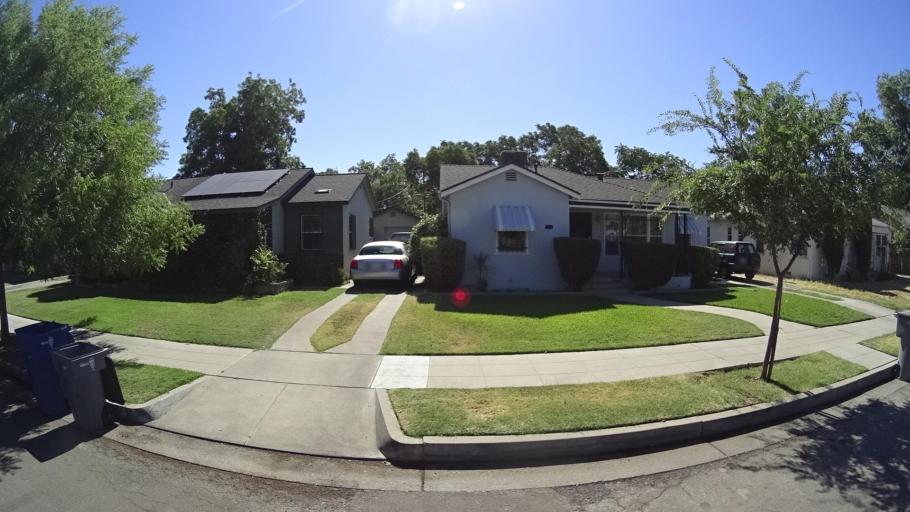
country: US
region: California
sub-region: Fresno County
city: Fresno
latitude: 36.7167
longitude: -119.7874
